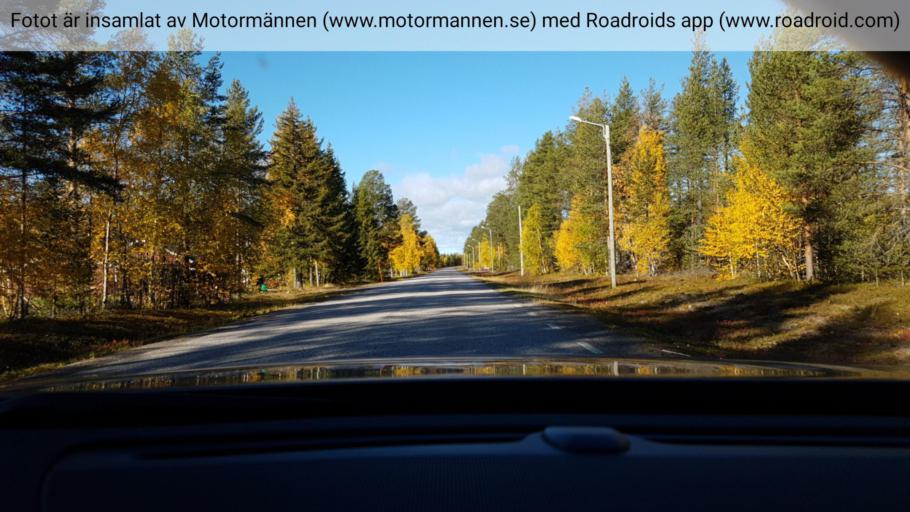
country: SE
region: Norrbotten
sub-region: Arvidsjaurs Kommun
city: Arvidsjaur
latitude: 65.6821
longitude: 18.8107
